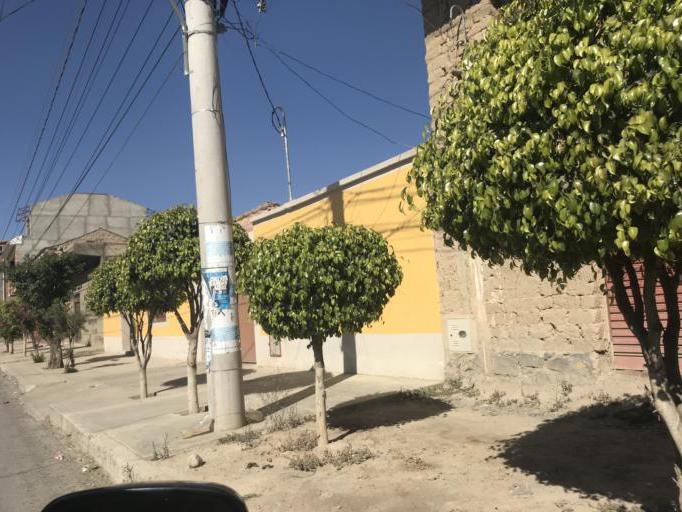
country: BO
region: Cochabamba
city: Punata
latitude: -17.5484
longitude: -65.8421
